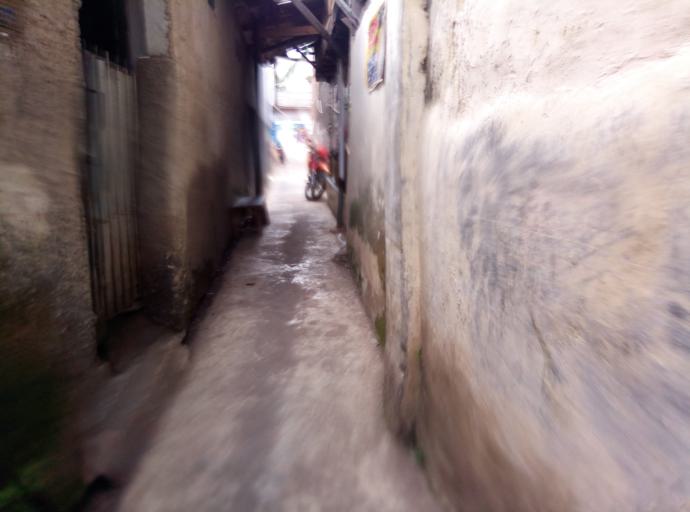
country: ID
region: West Java
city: Bandung
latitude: -6.9257
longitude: 107.6457
